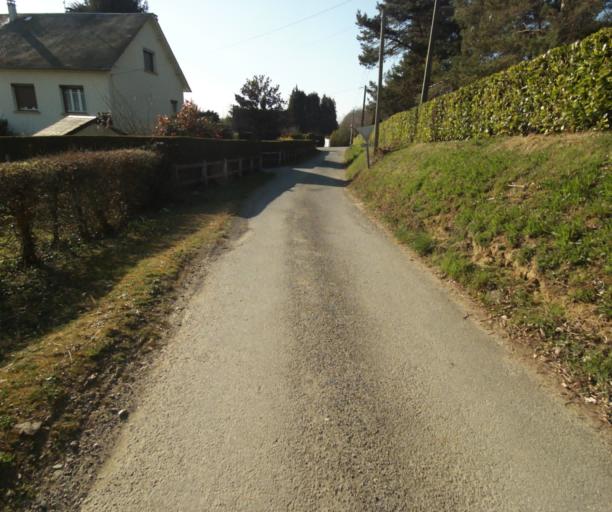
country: FR
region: Limousin
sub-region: Departement de la Correze
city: Saint-Clement
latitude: 45.3375
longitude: 1.6828
